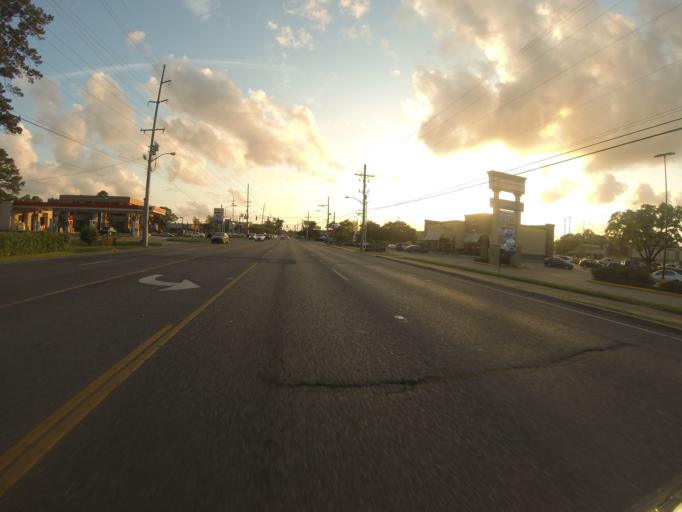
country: US
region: Louisiana
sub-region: Lafayette Parish
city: Lafayette
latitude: 30.2081
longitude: -92.0370
